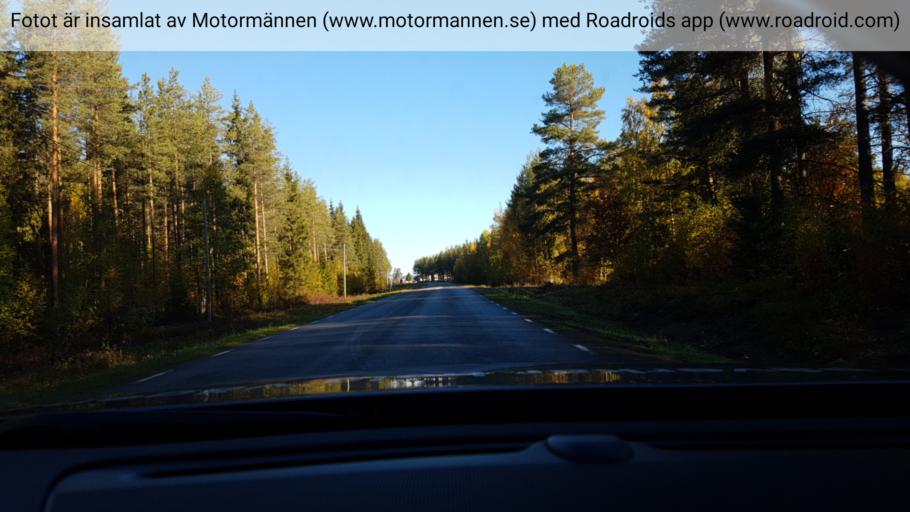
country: SE
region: Norrbotten
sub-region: Bodens Kommun
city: Boden
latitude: 65.8881
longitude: 21.6778
